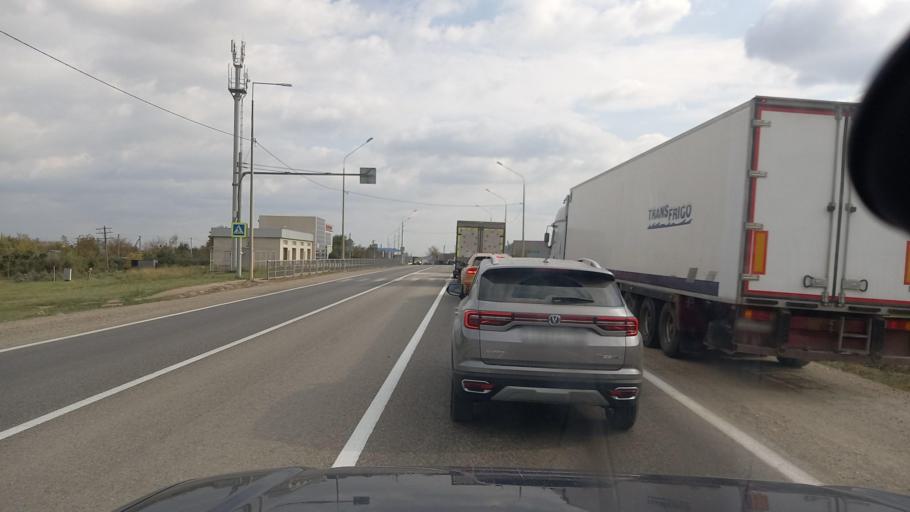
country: RU
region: Krasnodarskiy
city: Il'skiy
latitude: 44.8460
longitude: 38.5530
